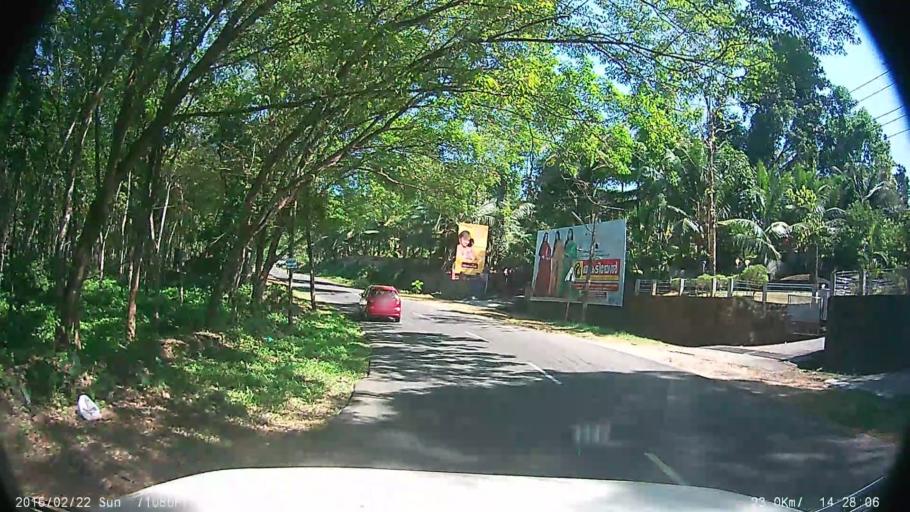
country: IN
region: Kerala
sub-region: Kottayam
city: Erattupetta
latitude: 9.5658
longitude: 76.7386
